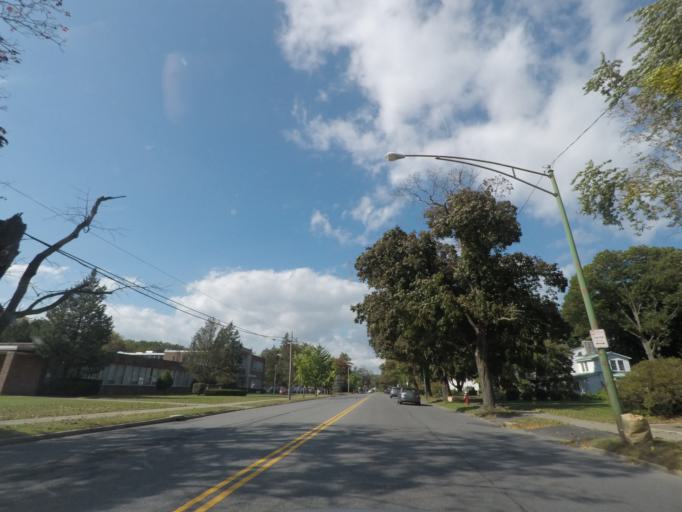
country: US
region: New York
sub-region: Albany County
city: West Albany
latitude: 42.6580
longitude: -73.8055
